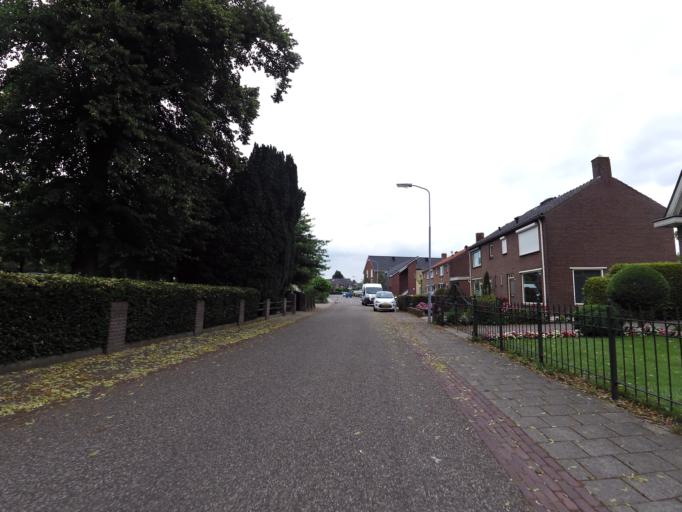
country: NL
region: Gelderland
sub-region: Gemeente Doesburg
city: Doesburg
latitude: 51.9939
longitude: 6.1299
